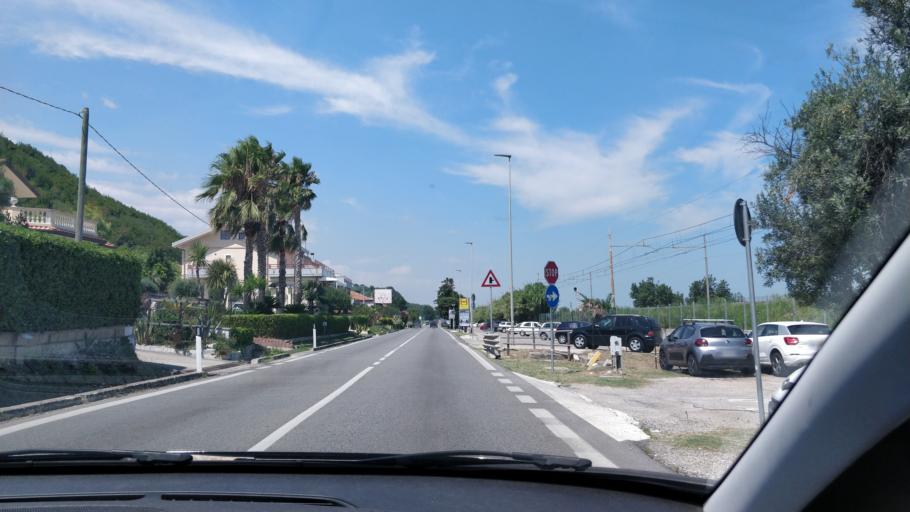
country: IT
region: Abruzzo
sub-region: Provincia di Chieti
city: Tollo
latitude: 42.3821
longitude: 14.3624
